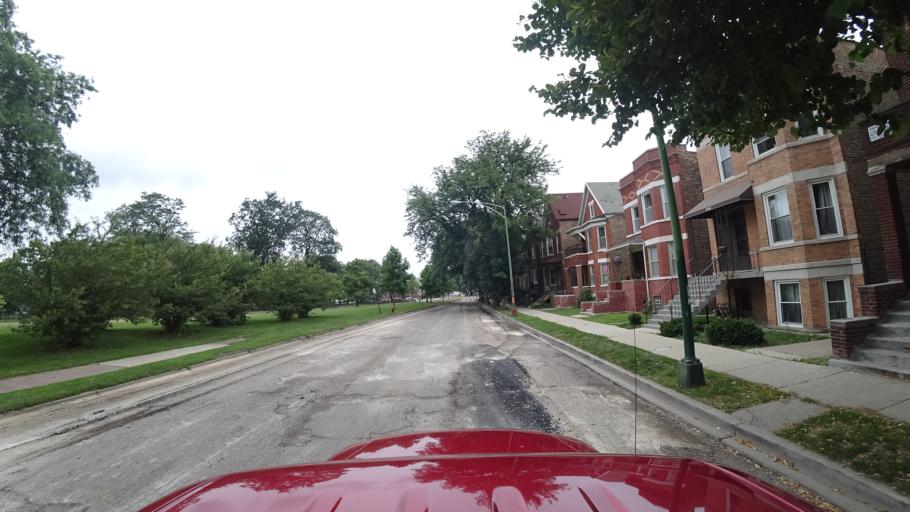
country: US
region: Illinois
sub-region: Cook County
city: Chicago
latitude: 41.8254
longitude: -87.6751
